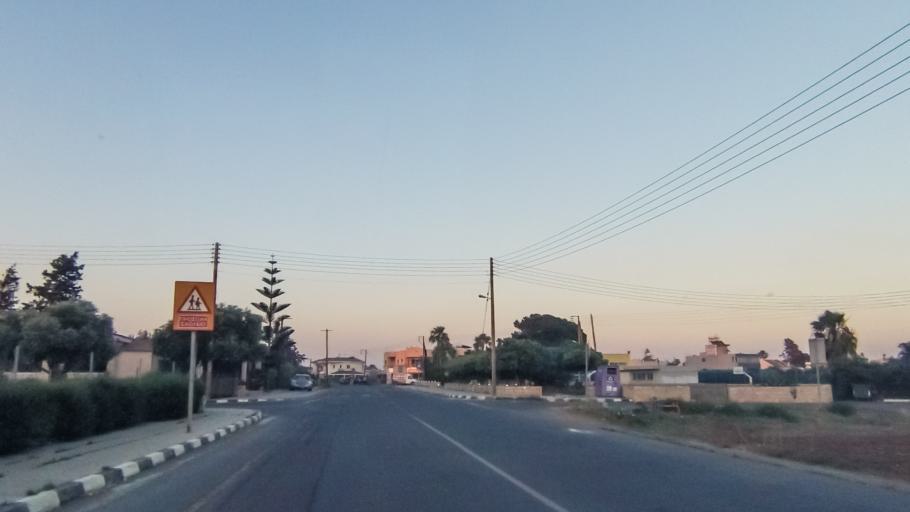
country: CY
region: Larnaka
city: Kolossi
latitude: 34.6385
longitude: 32.9596
